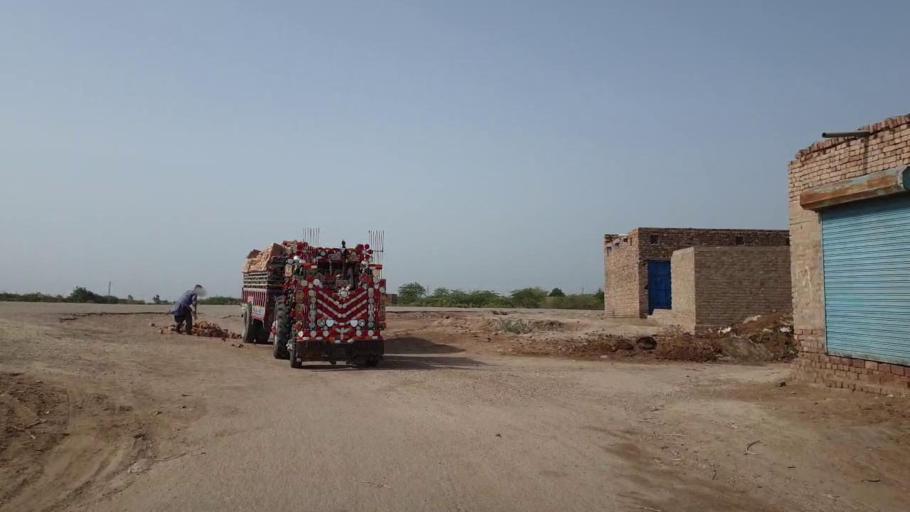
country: PK
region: Sindh
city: Jam Sahib
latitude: 26.2963
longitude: 68.6358
